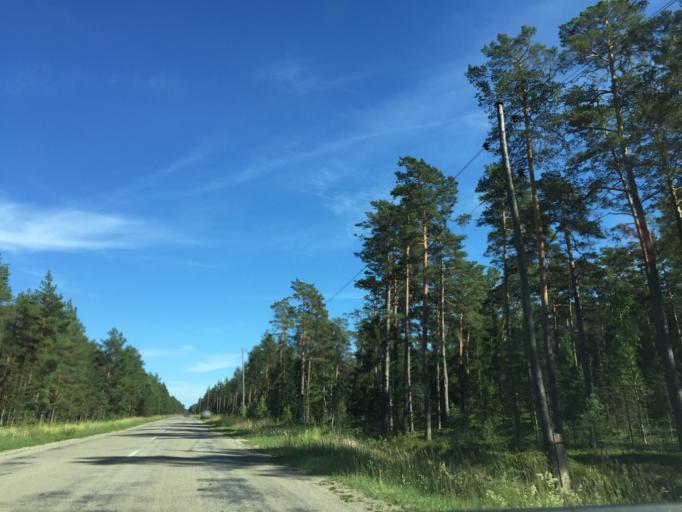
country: LV
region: Mesraga
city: Mersrags
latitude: 57.3957
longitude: 22.9846
